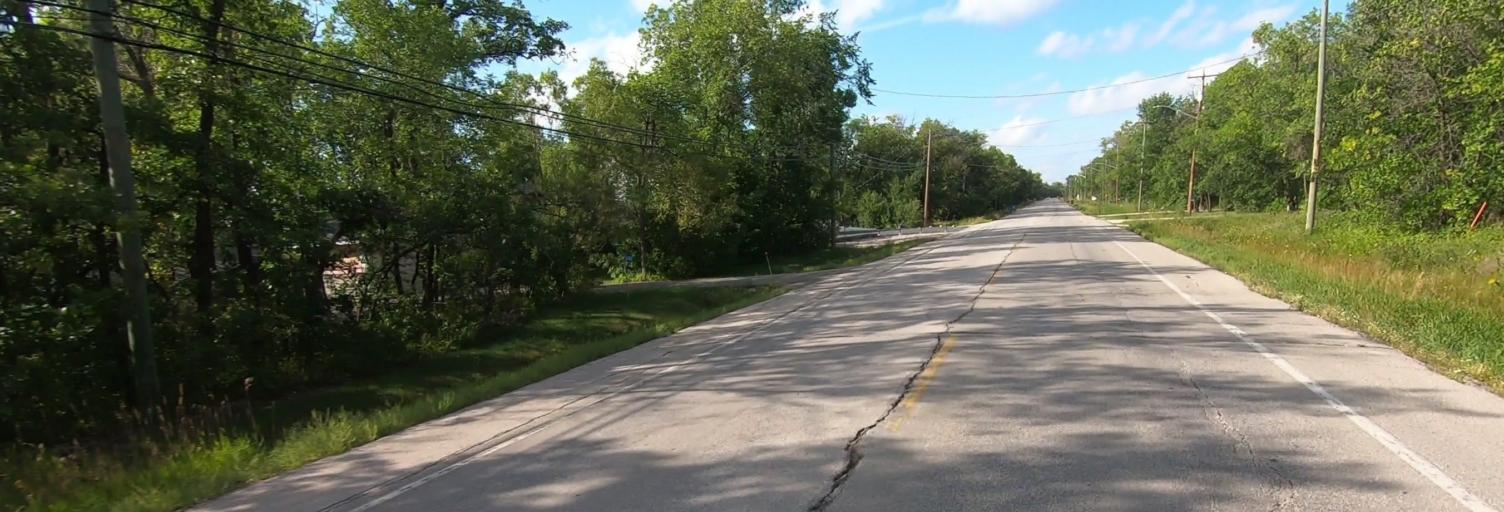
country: CA
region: Manitoba
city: Winnipeg
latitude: 49.9995
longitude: -97.0376
